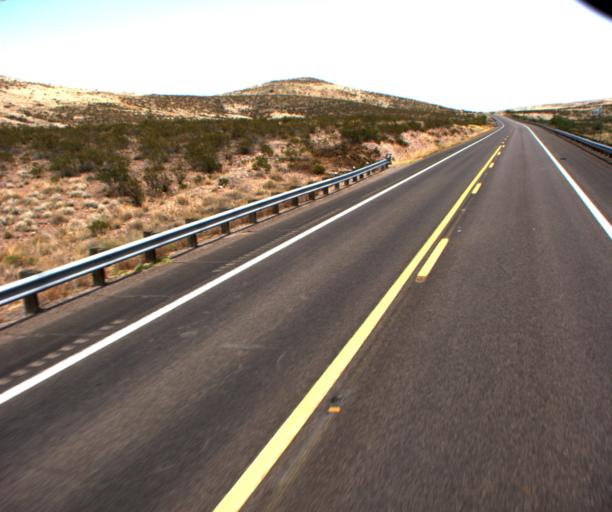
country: US
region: Arizona
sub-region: Greenlee County
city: Clifton
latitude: 32.7375
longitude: -109.1998
